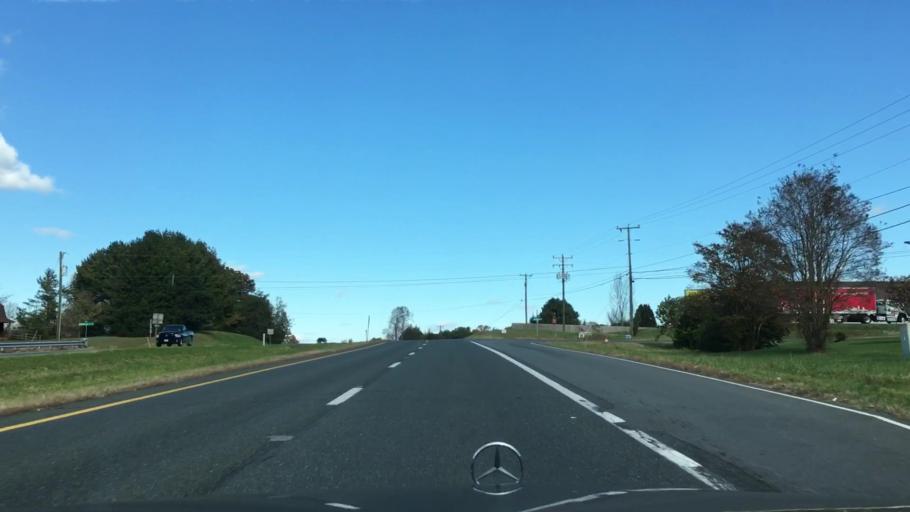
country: US
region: Virginia
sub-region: Campbell County
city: Altavista
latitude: 37.1841
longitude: -79.2040
